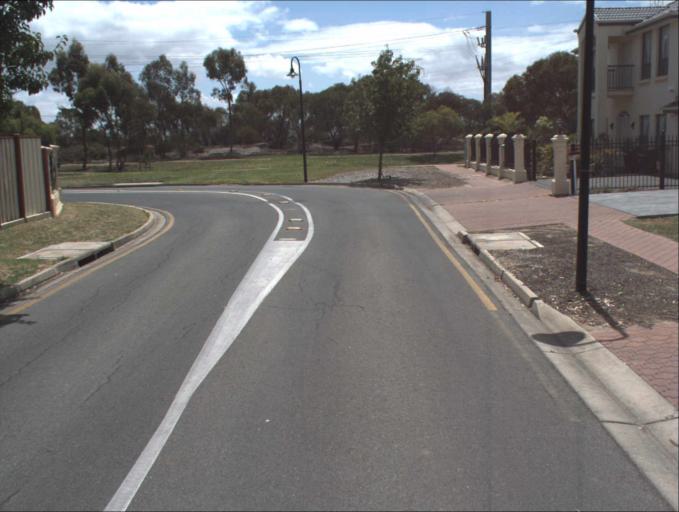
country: AU
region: South Australia
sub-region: Salisbury
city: Ingle Farm
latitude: -34.8482
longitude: 138.6329
